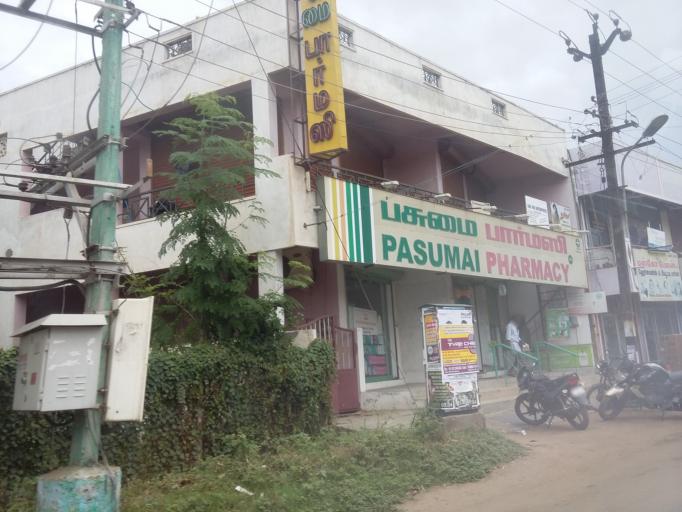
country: IN
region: Tamil Nadu
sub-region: Coimbatore
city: Perur
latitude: 11.0197
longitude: 76.9192
